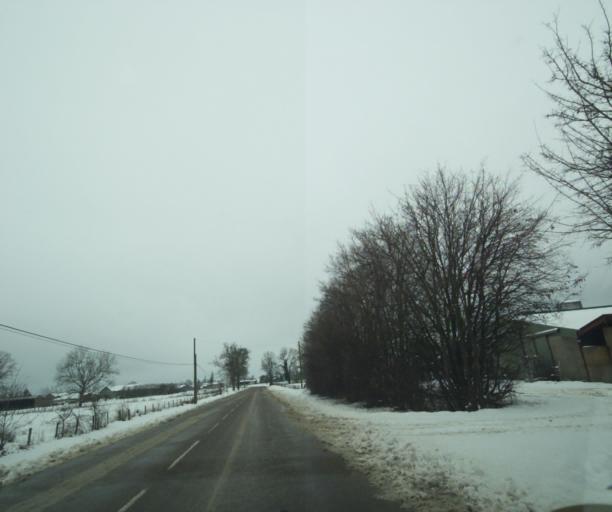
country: FR
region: Champagne-Ardenne
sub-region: Departement de la Haute-Marne
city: Montier-en-Der
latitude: 48.4537
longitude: 4.7738
